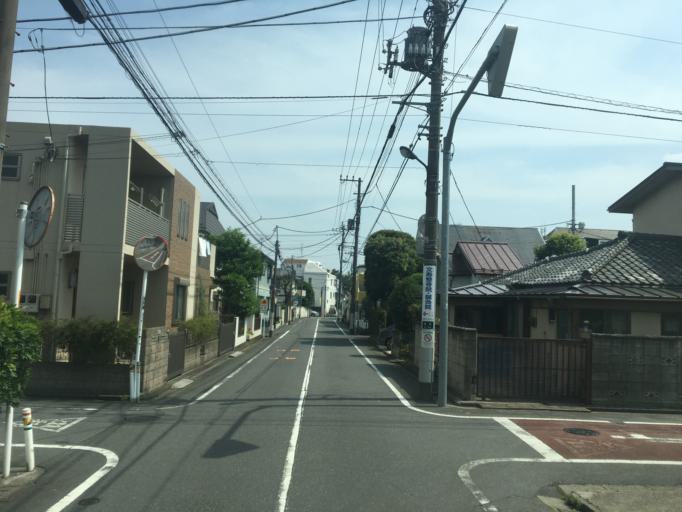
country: JP
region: Tokyo
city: Tokyo
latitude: 35.7372
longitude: 139.6942
